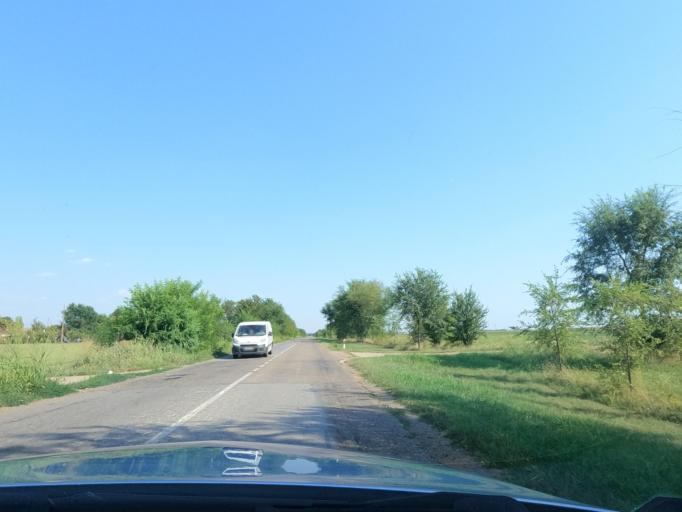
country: RS
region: Autonomna Pokrajina Vojvodina
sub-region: Juznobacki Okrug
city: Becej
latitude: 45.6471
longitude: 19.9830
